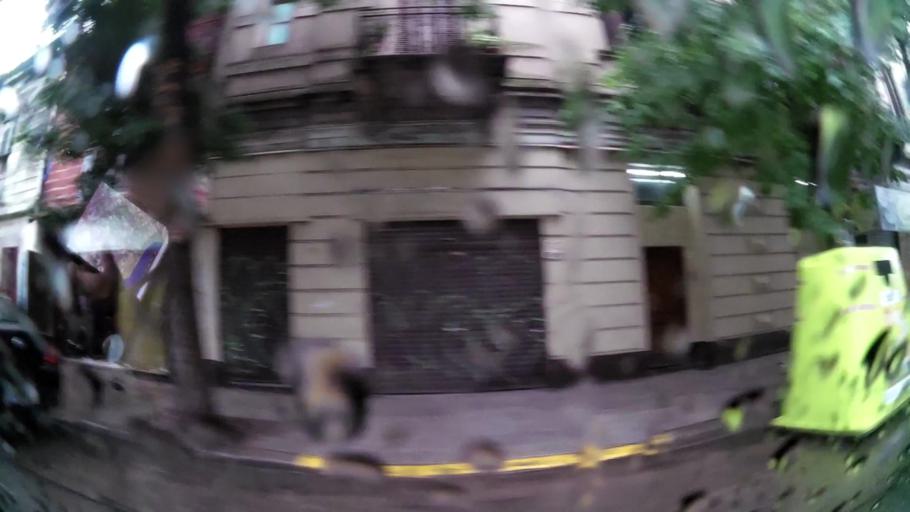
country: AR
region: Buenos Aires
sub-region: Partido de Avellaneda
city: Avellaneda
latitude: -34.6371
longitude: -58.3614
